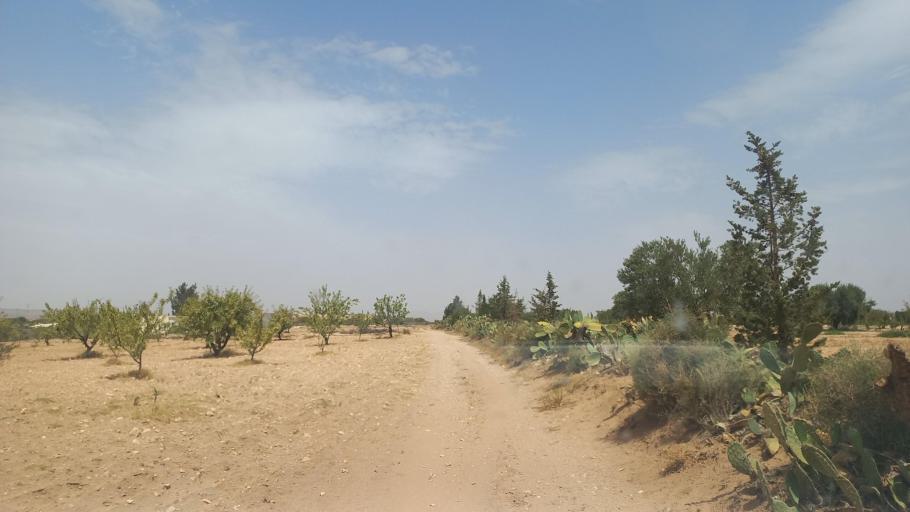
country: TN
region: Al Qasrayn
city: Kasserine
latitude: 35.2624
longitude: 8.9864
